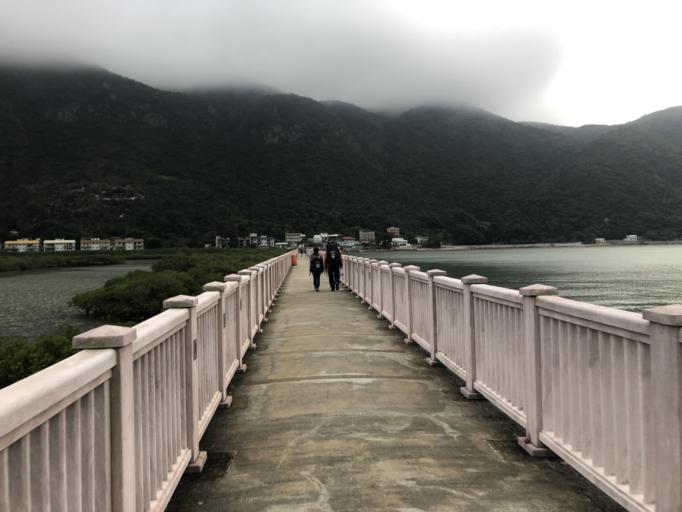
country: HK
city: Tai O
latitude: 22.2504
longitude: 113.8609
